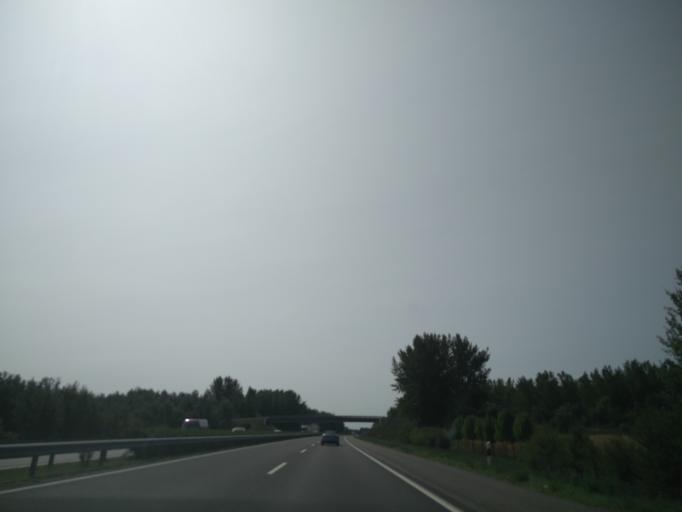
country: HU
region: Bacs-Kiskun
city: Kiskunfelegyhaza
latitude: 46.6623
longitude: 19.8313
